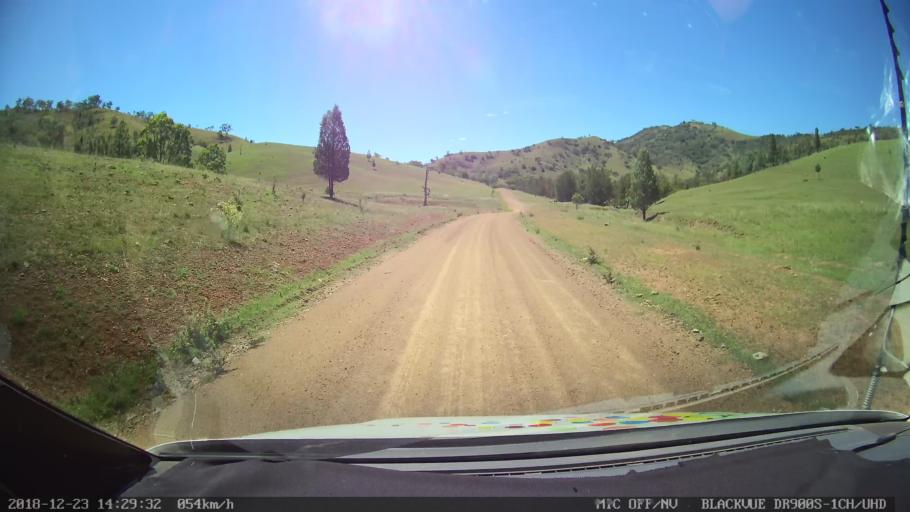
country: AU
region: New South Wales
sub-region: Tamworth Municipality
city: Manilla
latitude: -30.6079
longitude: 150.9373
